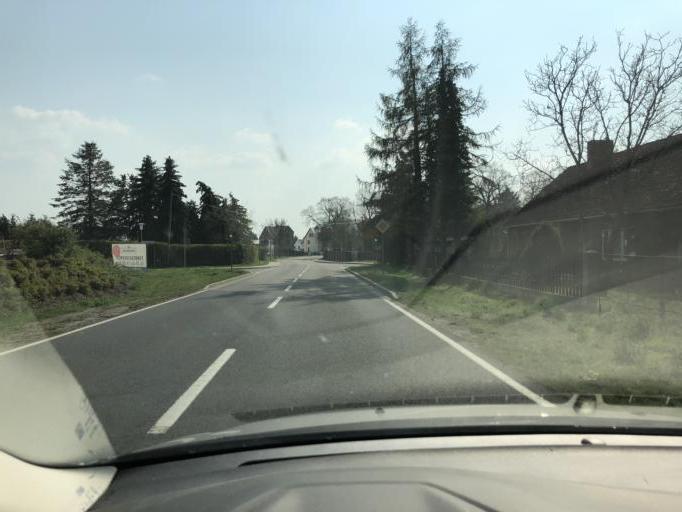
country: DE
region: Saxony-Anhalt
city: Grobers
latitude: 51.4483
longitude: 12.1171
